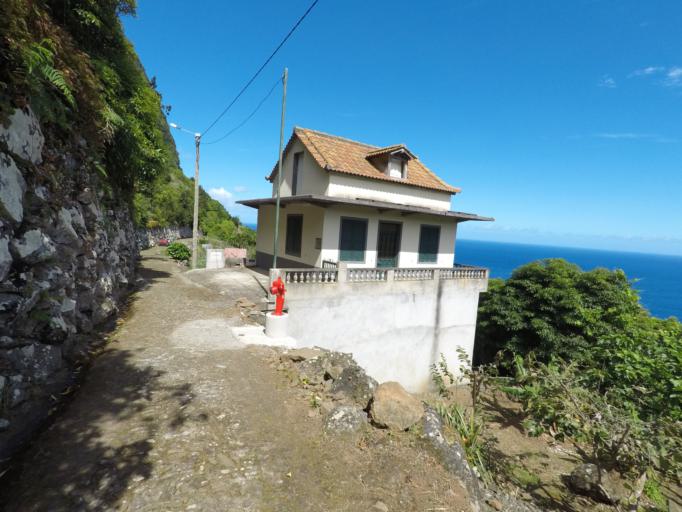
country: PT
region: Madeira
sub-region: Santana
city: Santana
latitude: 32.8248
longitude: -16.9610
